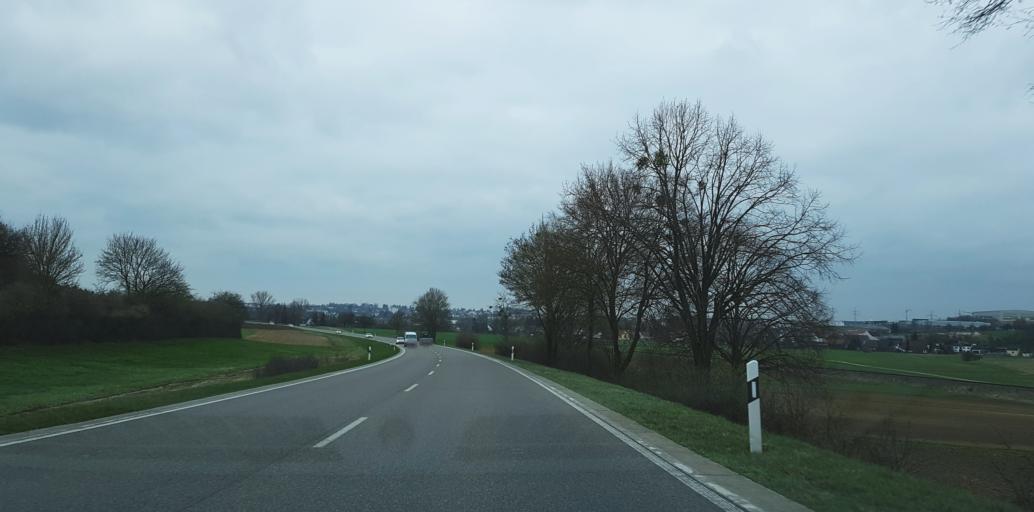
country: DE
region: Baden-Wuerttemberg
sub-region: Tuebingen Region
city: Allmendingen
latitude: 48.3080
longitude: 9.7227
